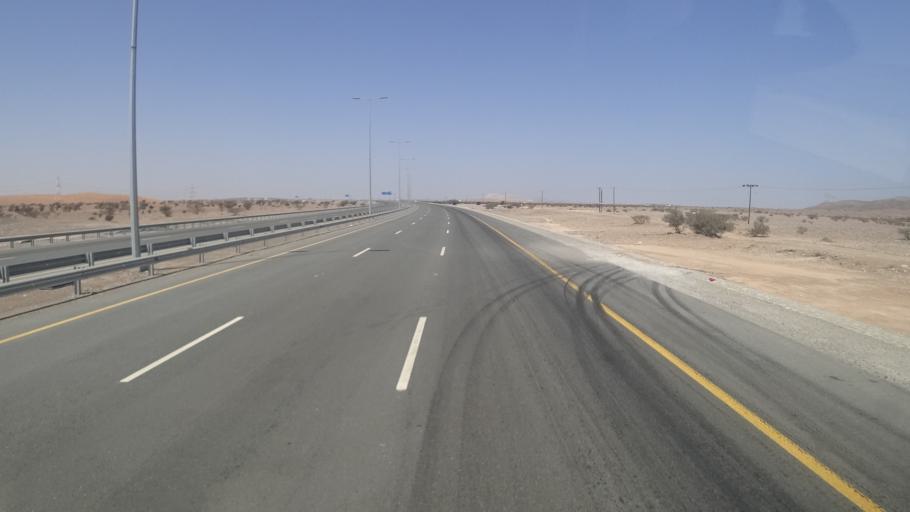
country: OM
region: Ash Sharqiyah
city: Badiyah
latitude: 22.4938
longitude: 58.9660
